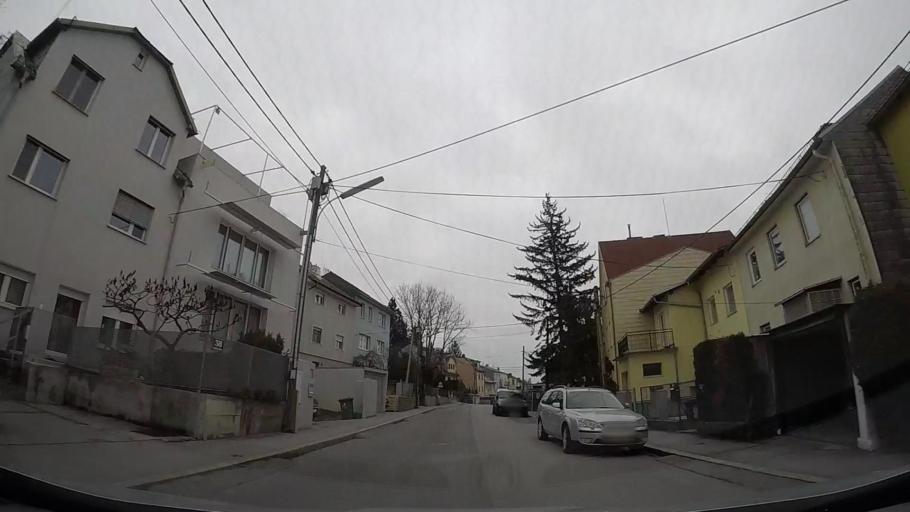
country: AT
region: Lower Austria
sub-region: Politischer Bezirk Wien-Umgebung
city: Purkersdorf
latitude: 48.2076
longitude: 16.2485
